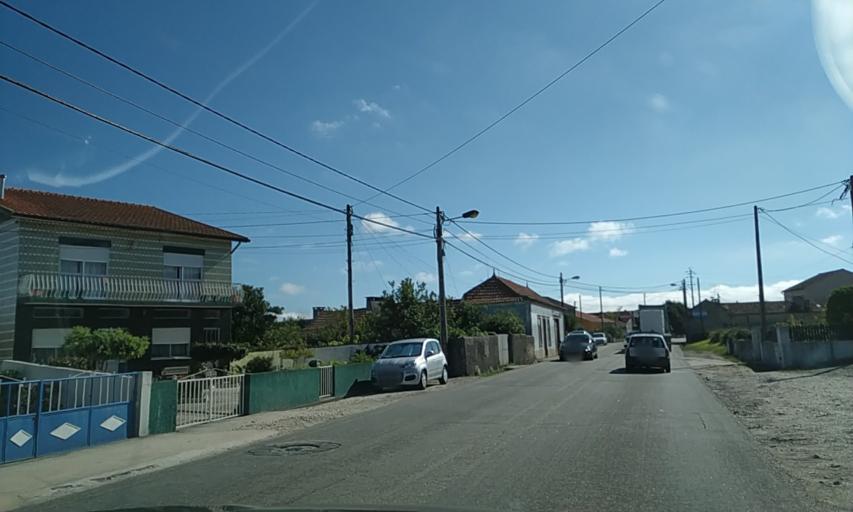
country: PT
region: Aveiro
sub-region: Aveiro
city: Aveiro
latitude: 40.6766
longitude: -8.5999
